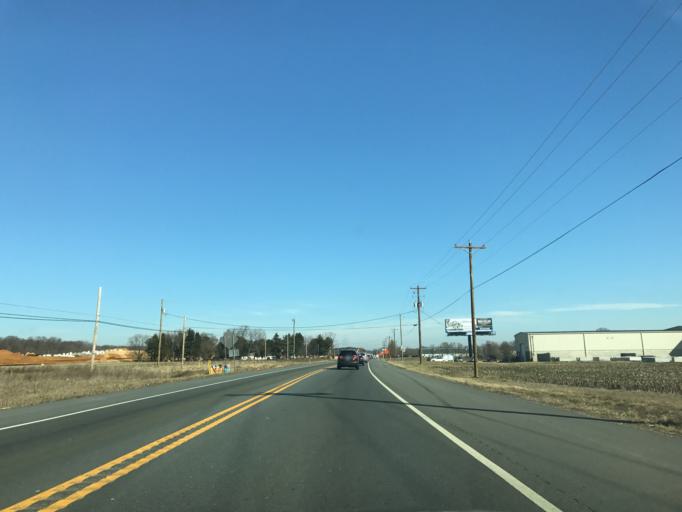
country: US
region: Delaware
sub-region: New Castle County
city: Middletown
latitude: 39.4822
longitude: -75.7198
